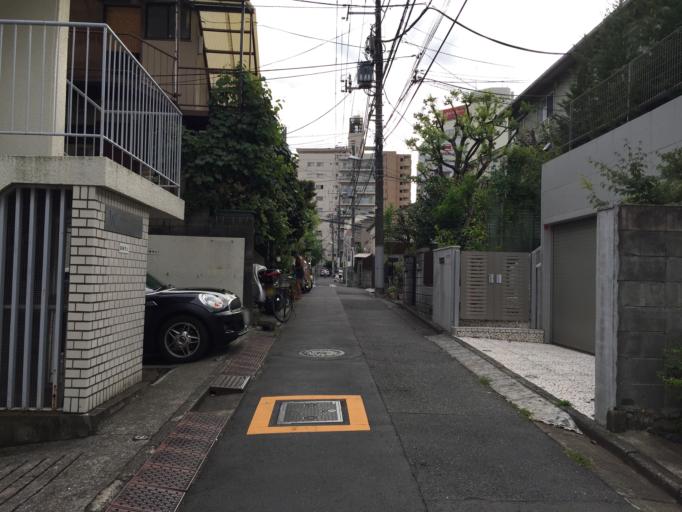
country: JP
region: Tokyo
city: Tokyo
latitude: 35.6581
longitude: 139.6930
